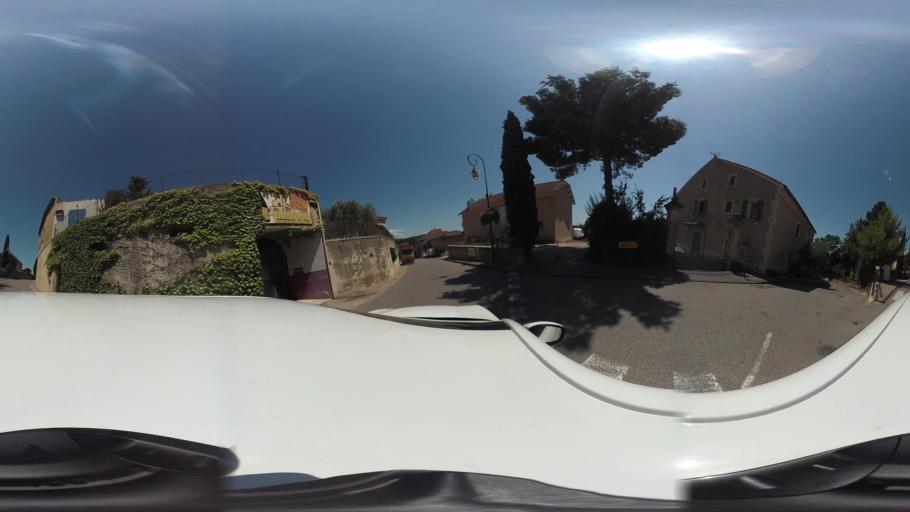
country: FR
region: Provence-Alpes-Cote d'Azur
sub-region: Departement du Vaucluse
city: Vacqueyras
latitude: 44.1378
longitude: 4.9817
